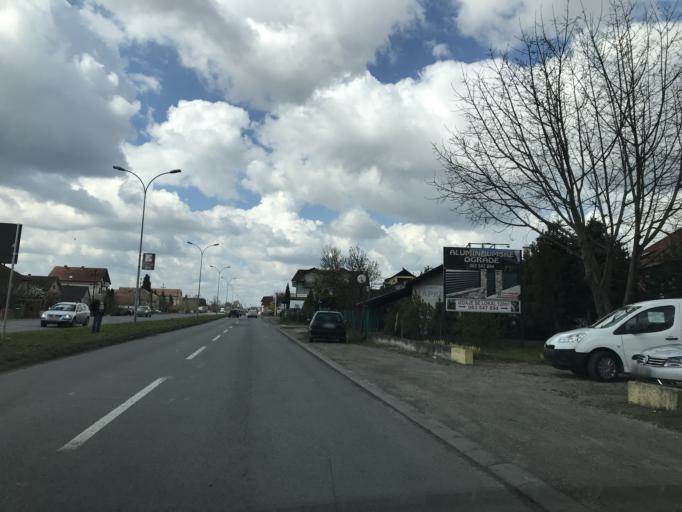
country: RS
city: Veternik
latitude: 45.2476
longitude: 19.7424
